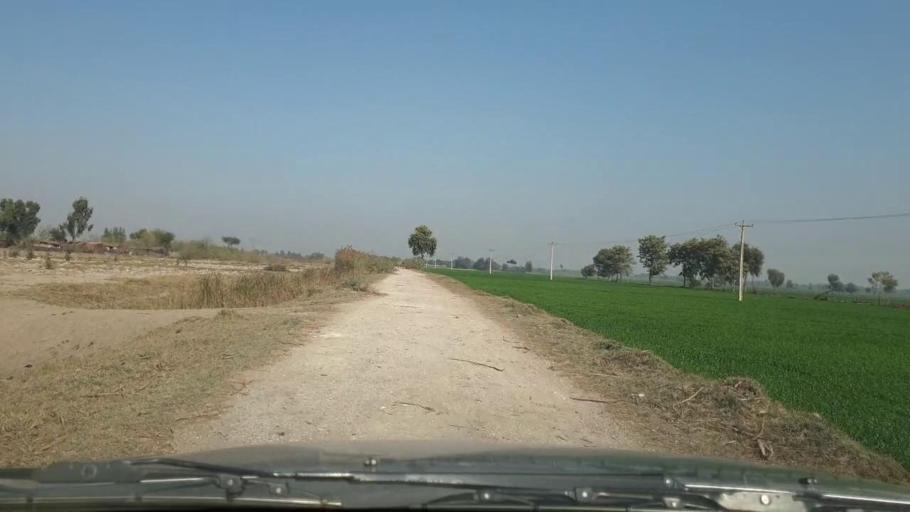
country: PK
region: Sindh
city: Mirpur Mathelo
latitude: 28.0415
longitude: 69.5598
